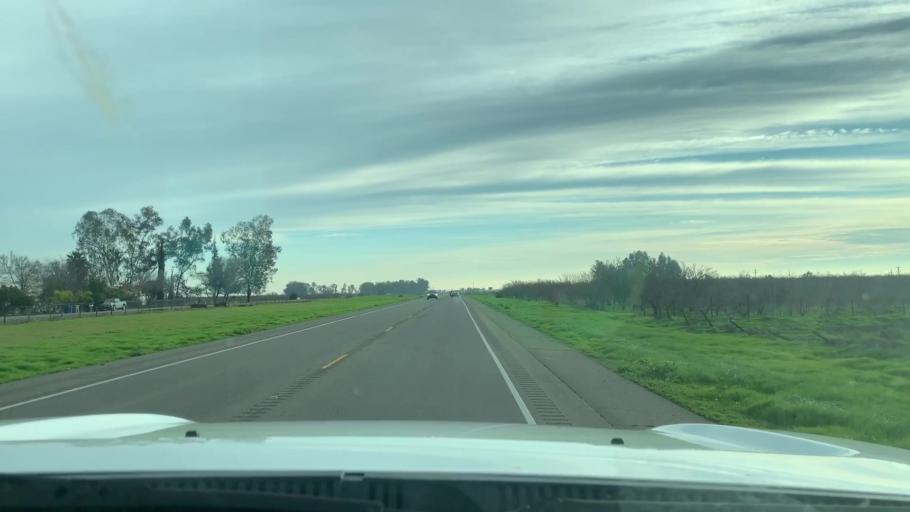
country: US
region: California
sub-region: Fresno County
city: Riverdale
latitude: 36.4723
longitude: -119.7938
